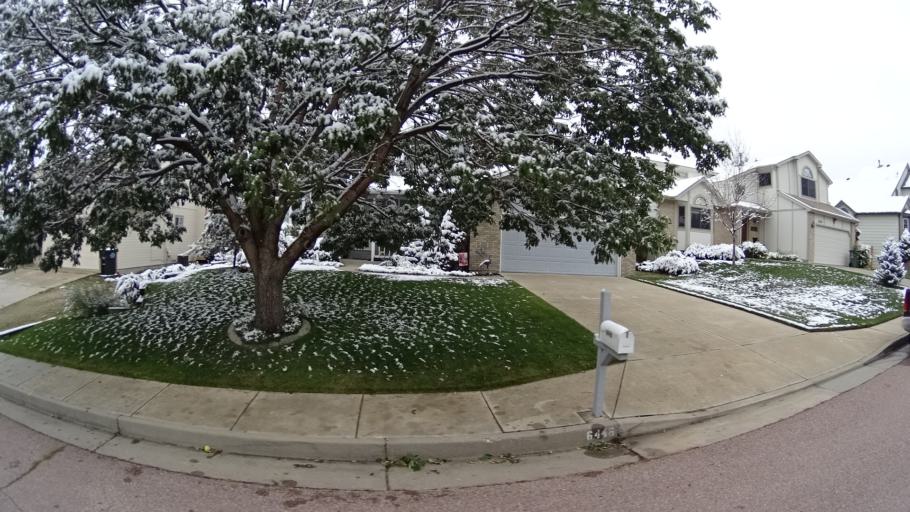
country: US
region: Colorado
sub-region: El Paso County
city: Colorado Springs
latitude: 38.9246
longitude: -104.7815
